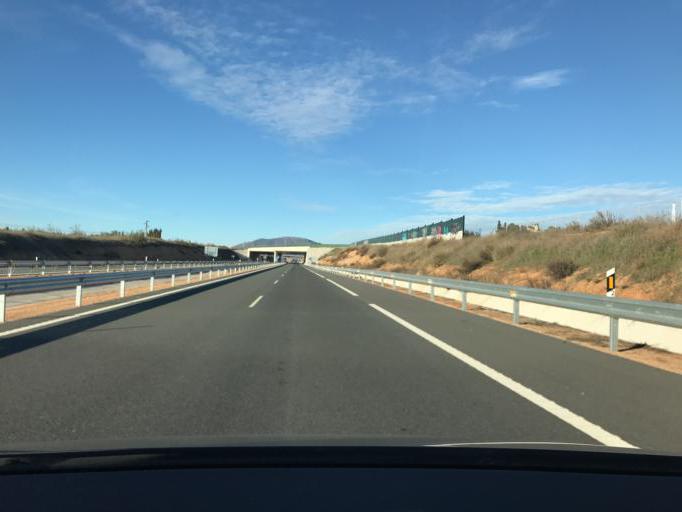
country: ES
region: Andalusia
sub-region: Provincia de Granada
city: Albolote
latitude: 37.2443
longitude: -3.6624
